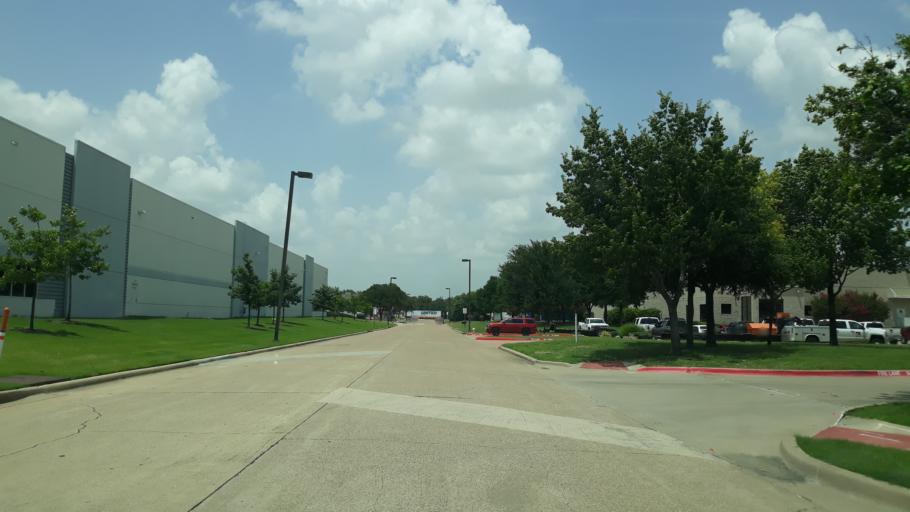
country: US
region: Texas
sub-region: Dallas County
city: Coppell
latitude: 32.9368
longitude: -97.0004
